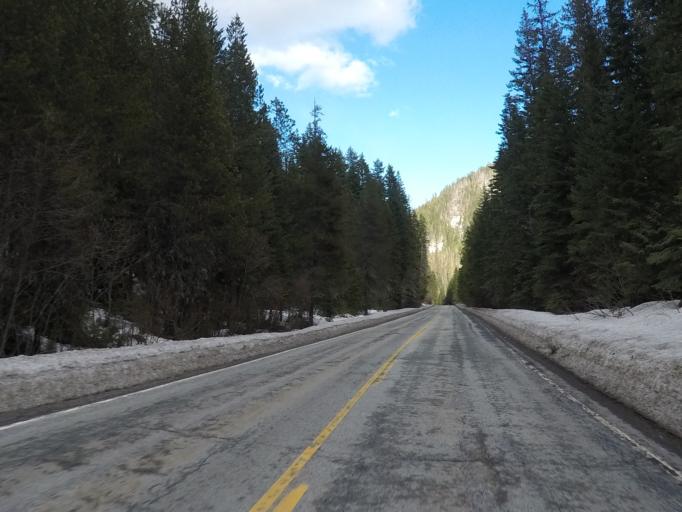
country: US
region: Montana
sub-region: Mineral County
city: Superior
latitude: 46.4870
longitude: -114.8778
